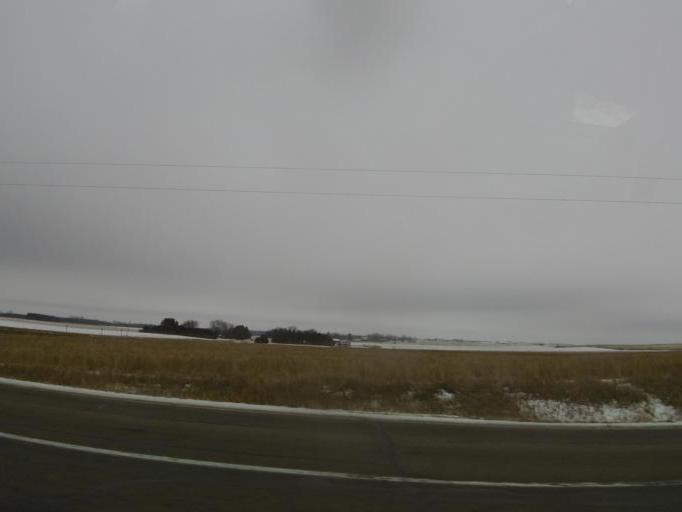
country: US
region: Iowa
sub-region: Chickasaw County
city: New Hampton
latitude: 43.1834
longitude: -92.2985
